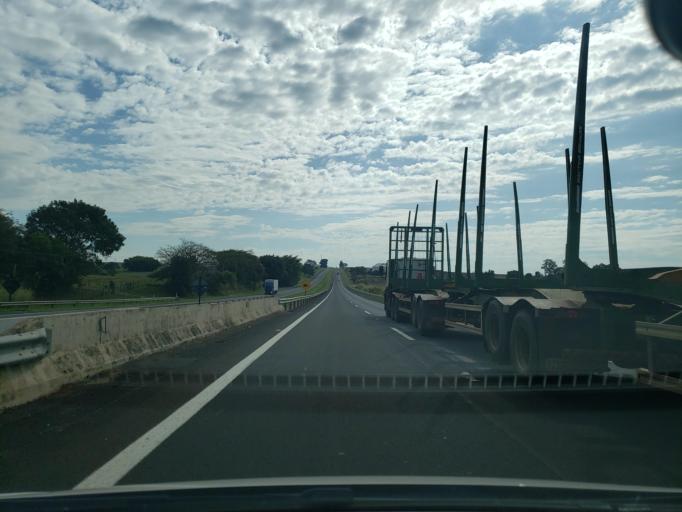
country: BR
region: Sao Paulo
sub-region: Lins
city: Lins
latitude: -21.6483
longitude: -49.8148
